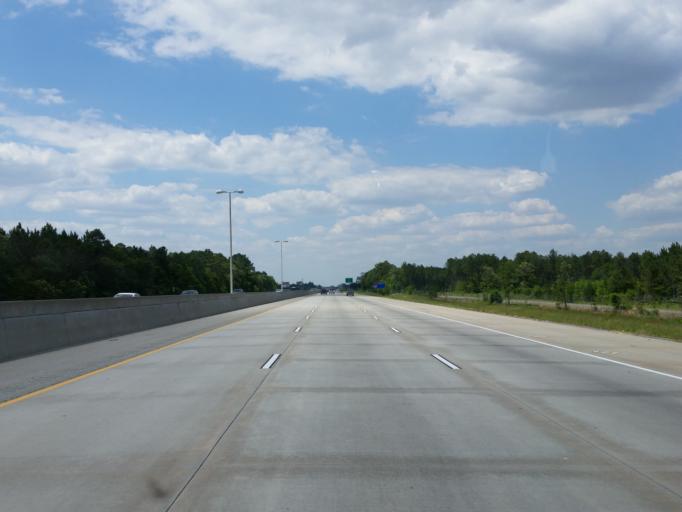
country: US
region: Georgia
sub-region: Cook County
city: Adel
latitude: 31.0924
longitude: -83.4170
